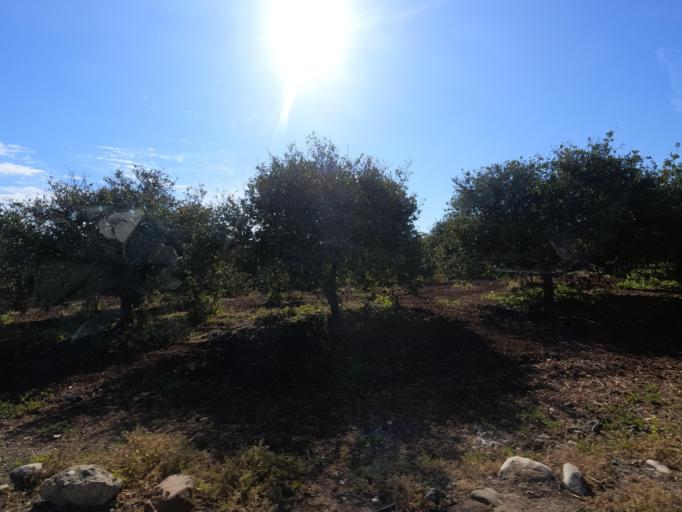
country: CY
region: Pafos
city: Polis
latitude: 35.0320
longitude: 32.3941
